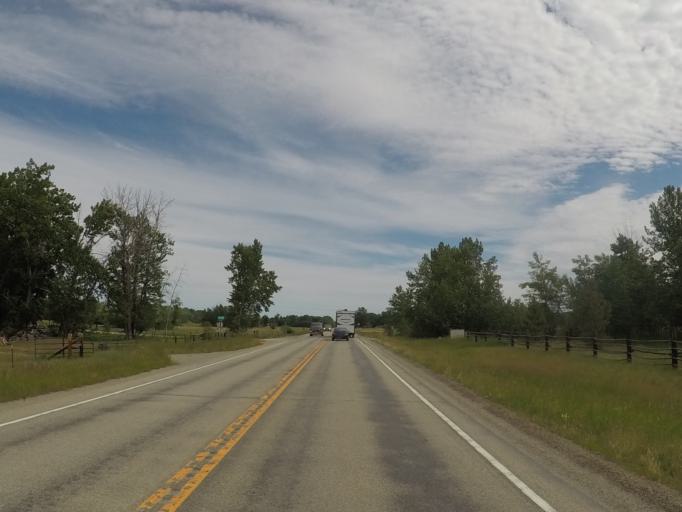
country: US
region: Montana
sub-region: Carbon County
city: Red Lodge
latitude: 45.2620
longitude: -109.2264
